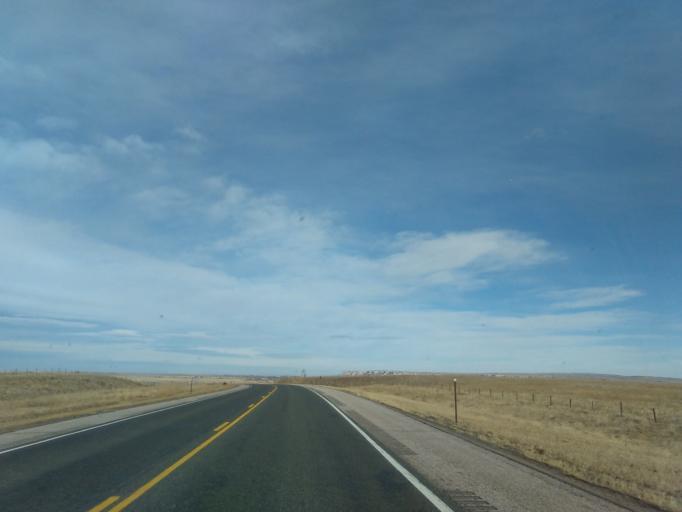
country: US
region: Wyoming
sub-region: Goshen County
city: Torrington
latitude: 41.6111
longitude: -104.2538
